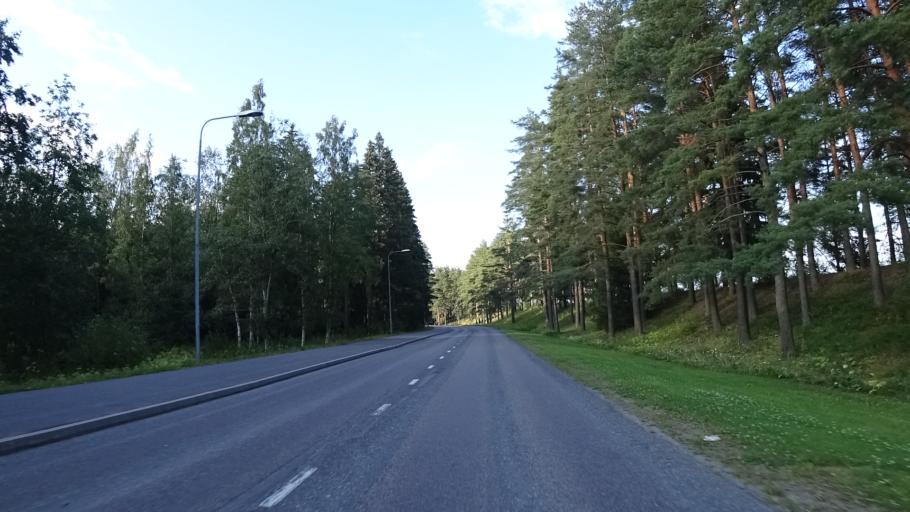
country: FI
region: South Karelia
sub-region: Imatra
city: Imatra
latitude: 61.1780
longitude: 28.7804
